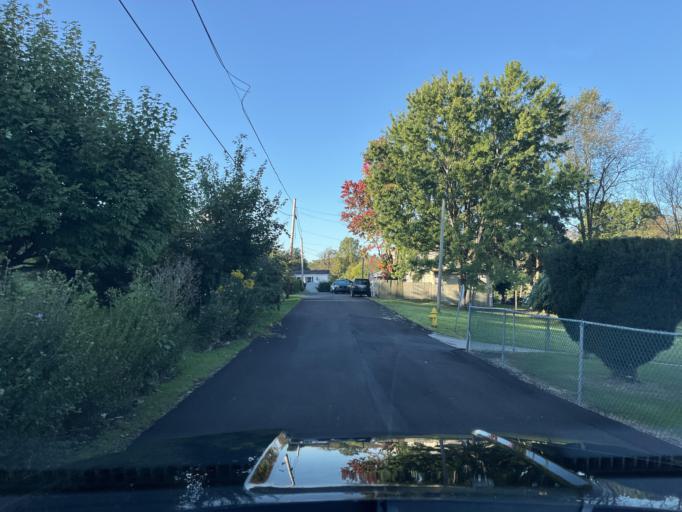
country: US
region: Pennsylvania
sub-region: Fayette County
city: Hopwood
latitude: 39.8582
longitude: -79.7169
